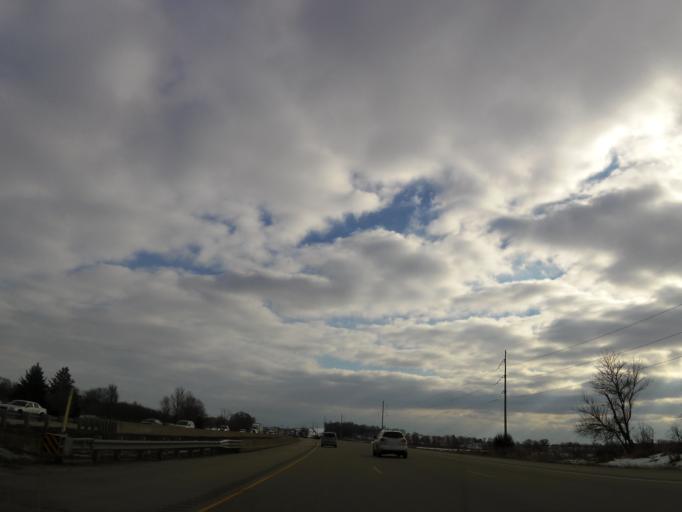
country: US
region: Wisconsin
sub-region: Dane County
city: Windsor
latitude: 43.2089
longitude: -89.3582
